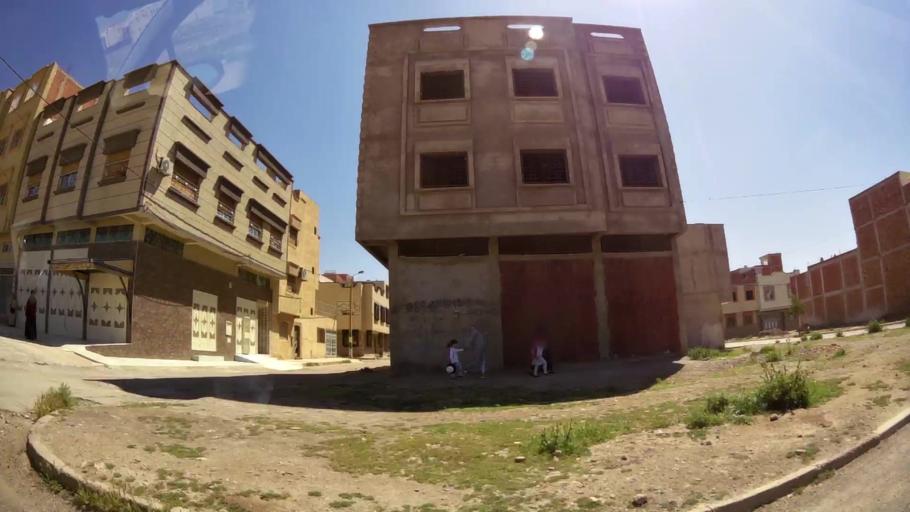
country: MA
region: Oriental
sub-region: Oujda-Angad
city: Oujda
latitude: 34.6906
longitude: -1.9330
